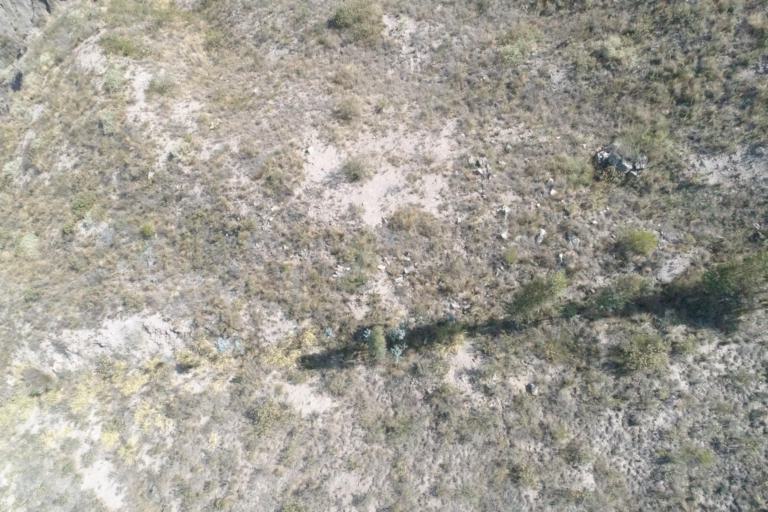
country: BO
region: La Paz
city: La Paz
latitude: -16.6225
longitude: -68.0393
